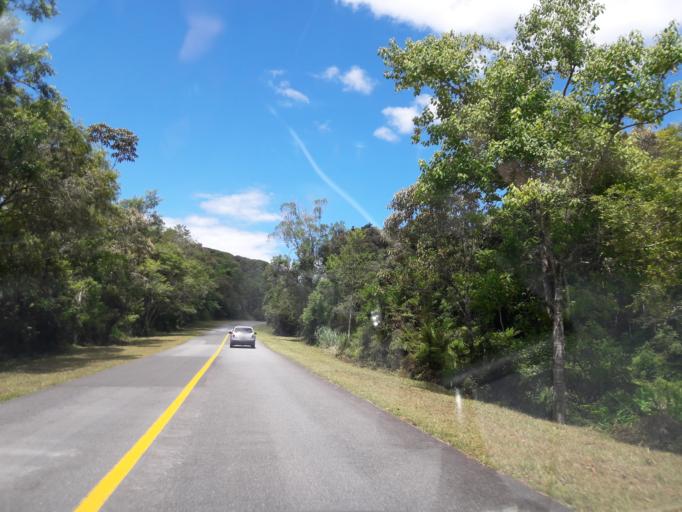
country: BR
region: Parana
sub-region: Antonina
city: Antonina
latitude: -25.4403
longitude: -48.7883
